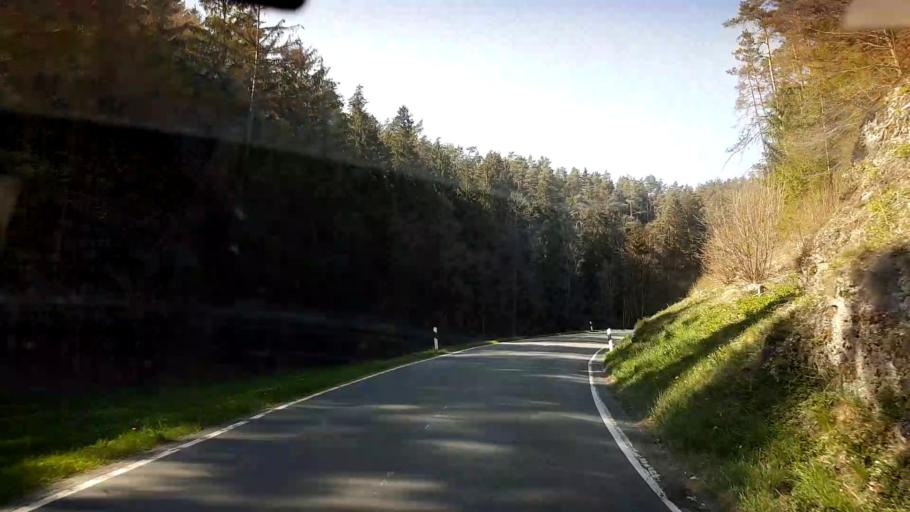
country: DE
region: Bavaria
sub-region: Upper Franconia
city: Pottenstein
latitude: 49.7807
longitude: 11.4191
